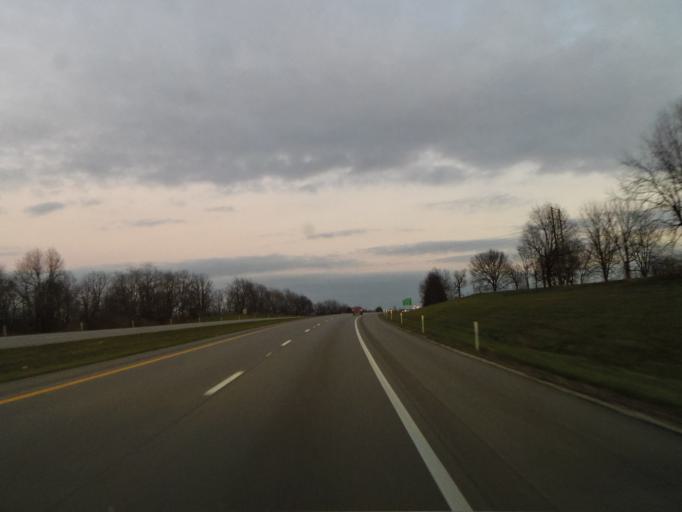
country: US
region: Kentucky
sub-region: Woodford County
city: Midway
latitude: 38.1627
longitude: -84.6274
